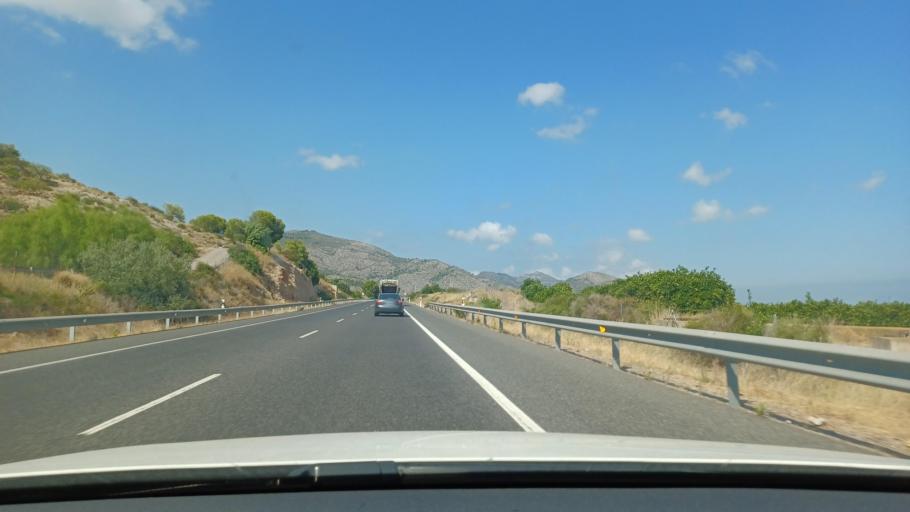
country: ES
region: Valencia
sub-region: Provincia de Castello
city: Borriol
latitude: 40.0238
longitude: -0.0371
